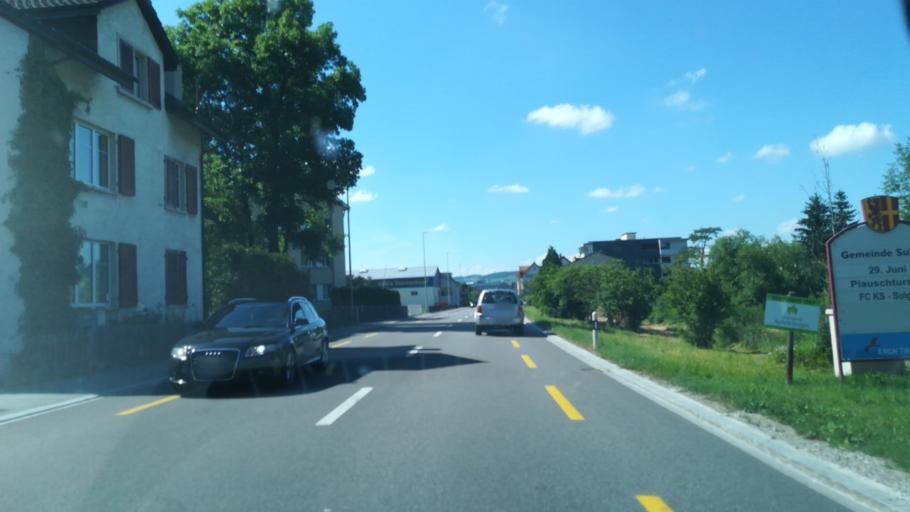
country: CH
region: Thurgau
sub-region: Weinfelden District
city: Sulgen
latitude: 47.5313
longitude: 9.1902
